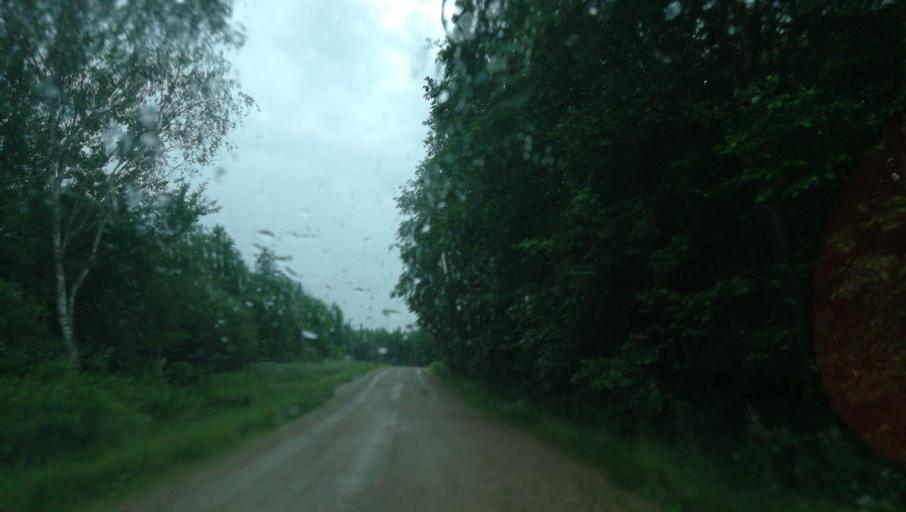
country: LV
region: Vecpiebalga
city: Vecpiebalga
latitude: 57.1041
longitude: 25.6921
